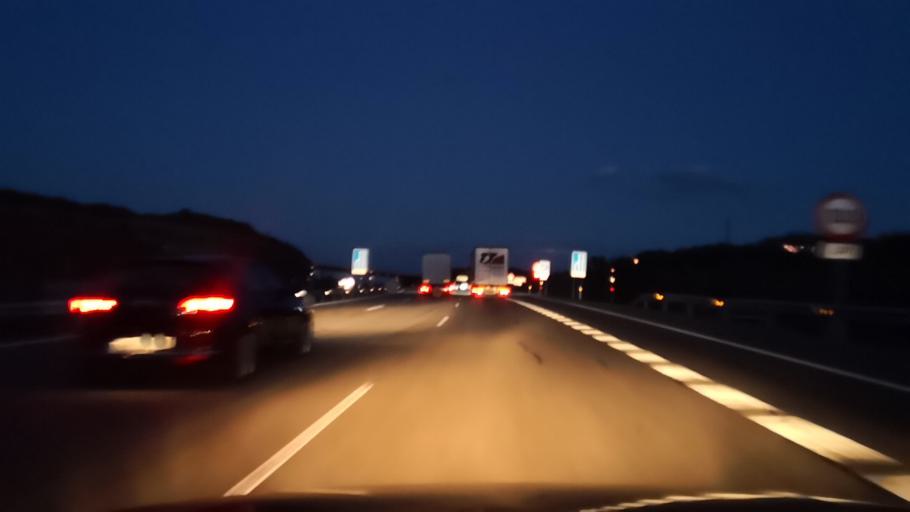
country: ES
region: Castille and Leon
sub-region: Provincia de Leon
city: Villagaton
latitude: 42.6010
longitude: -6.2361
